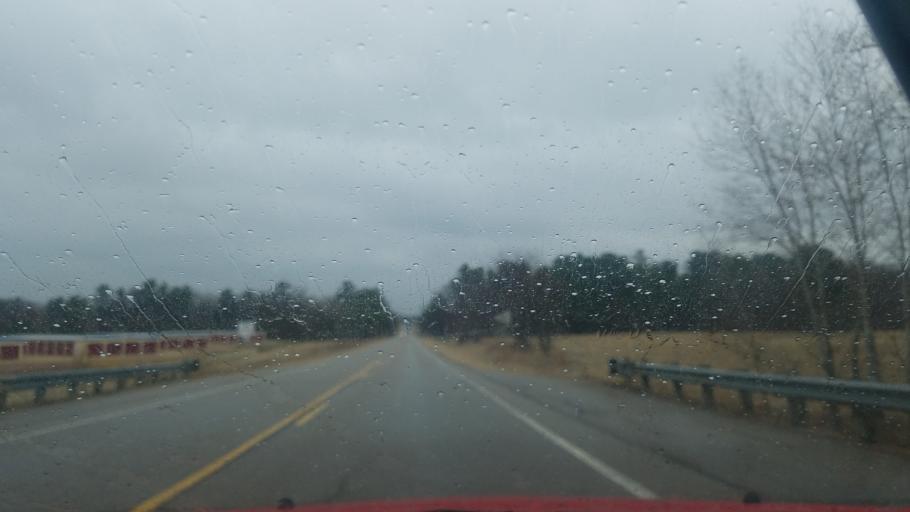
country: US
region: Wisconsin
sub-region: Dunn County
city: Tainter Lake
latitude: 44.9497
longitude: -91.9103
